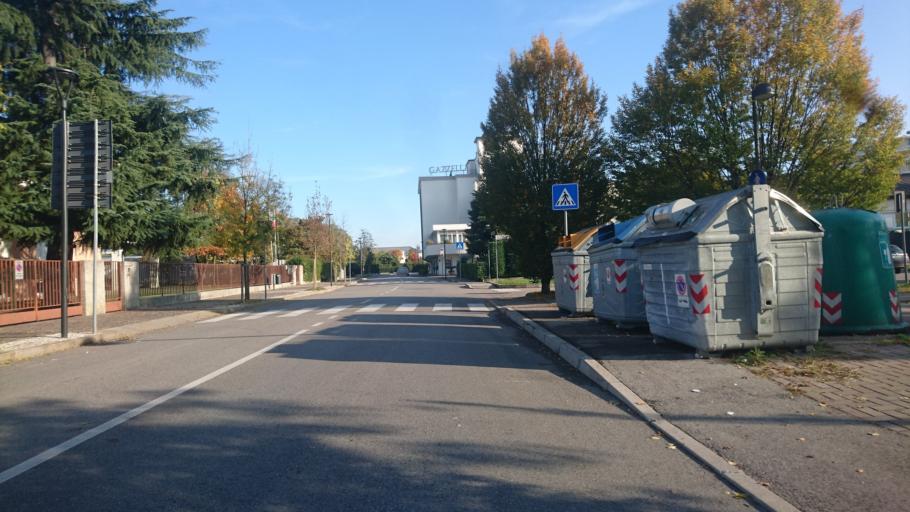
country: IT
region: Veneto
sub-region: Provincia di Padova
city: Abano Terme
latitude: 45.3482
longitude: 11.7809
